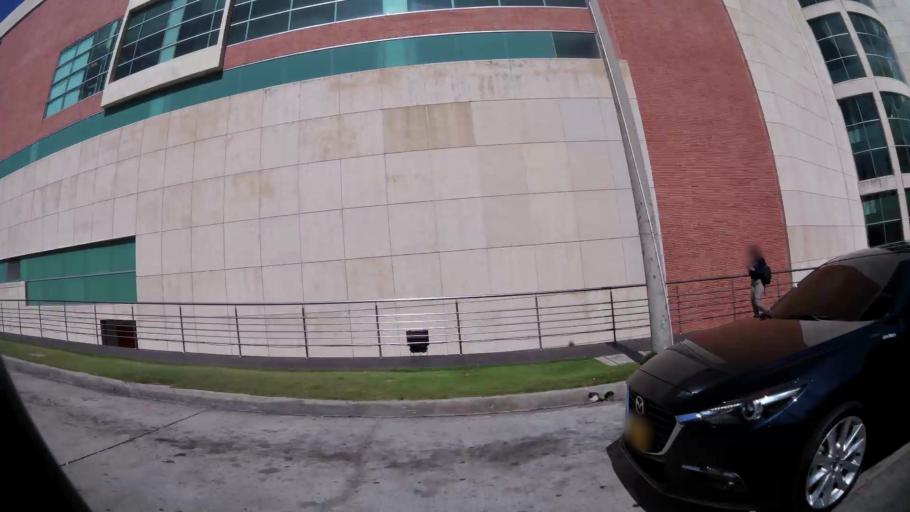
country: CO
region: Atlantico
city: Barranquilla
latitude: 11.0134
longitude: -74.8288
